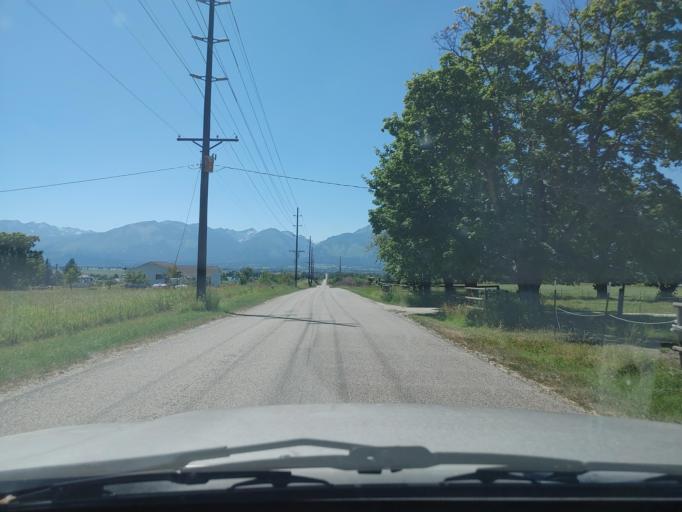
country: US
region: Montana
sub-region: Ravalli County
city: Hamilton
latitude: 46.2769
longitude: -114.0507
